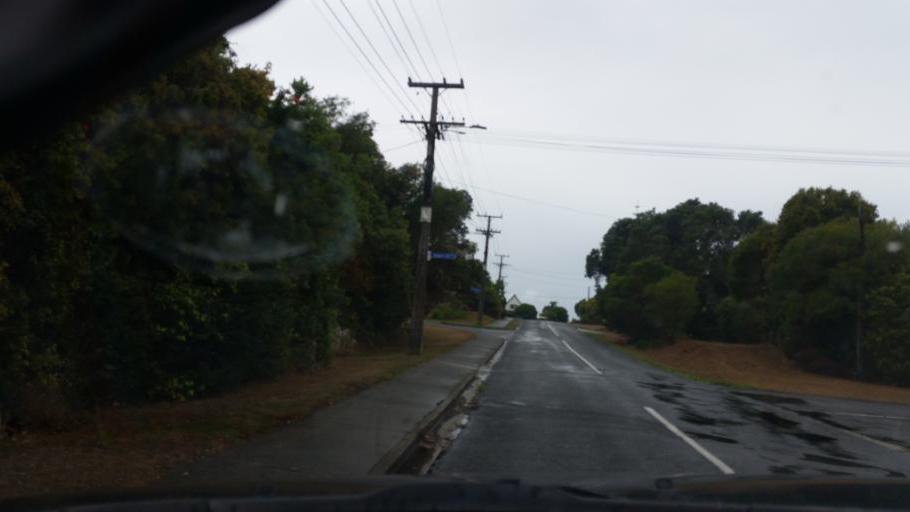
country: NZ
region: Auckland
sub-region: Auckland
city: Wellsford
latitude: -36.0940
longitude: 174.5889
